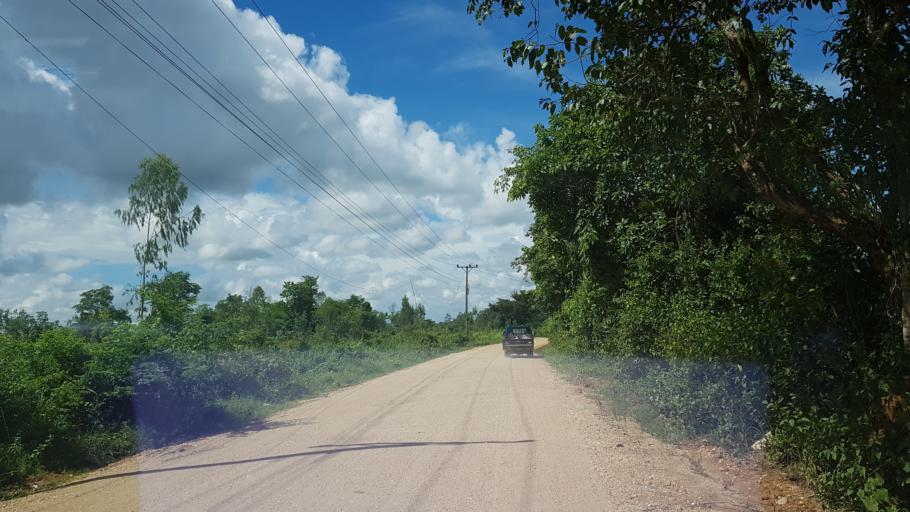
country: LA
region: Vientiane
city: Vientiane
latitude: 18.2306
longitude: 102.5257
